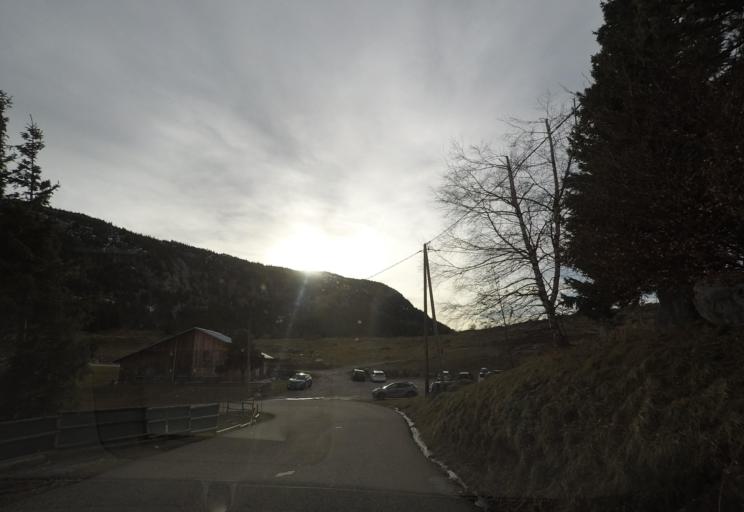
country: FR
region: Rhone-Alpes
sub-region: Departement de la Haute-Savoie
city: Bonneville
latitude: 46.0304
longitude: 6.4263
